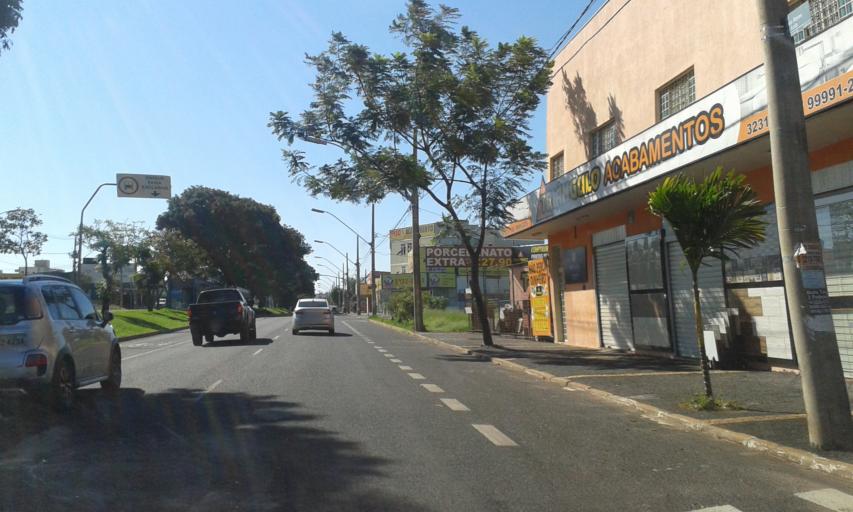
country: BR
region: Minas Gerais
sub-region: Uberlandia
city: Uberlandia
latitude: -18.9281
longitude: -48.2506
